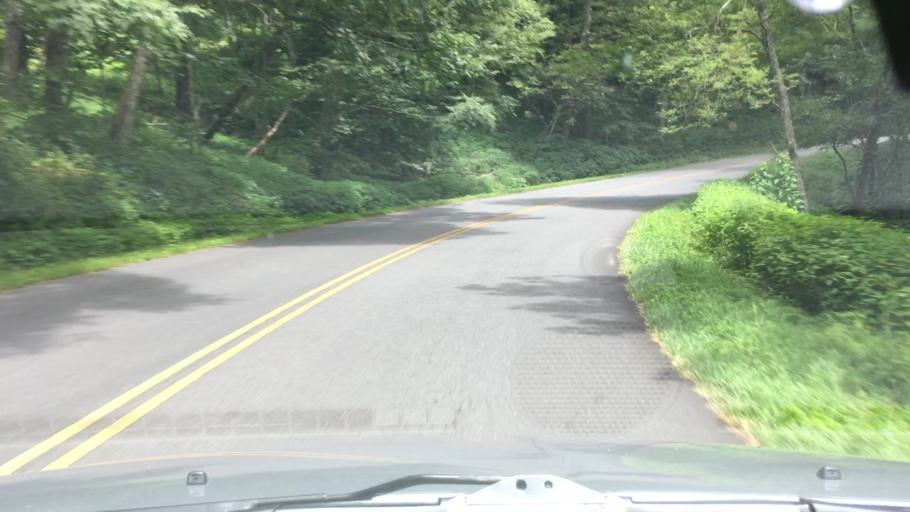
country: US
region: North Carolina
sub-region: Buncombe County
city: Swannanoa
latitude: 35.6790
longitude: -82.4296
